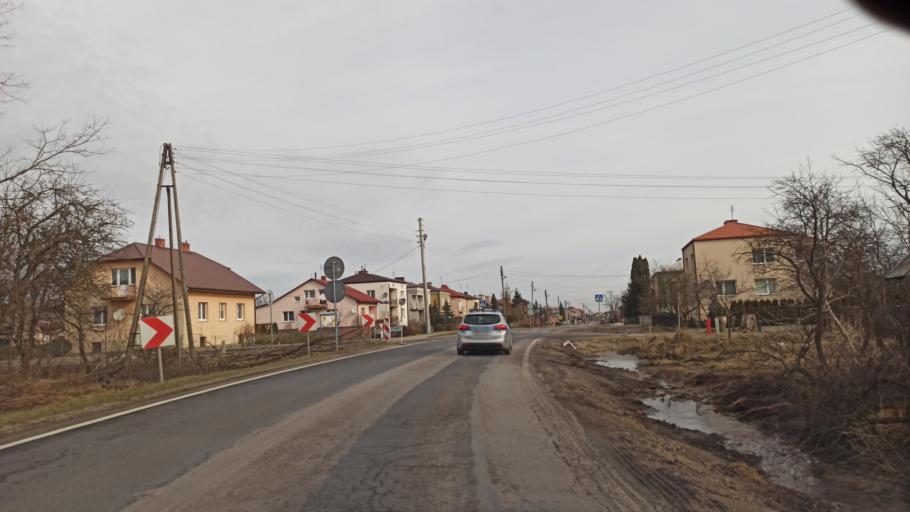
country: PL
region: Lublin Voivodeship
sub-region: Powiat bilgorajski
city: Tarnogrod
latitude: 50.3498
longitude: 22.7349
